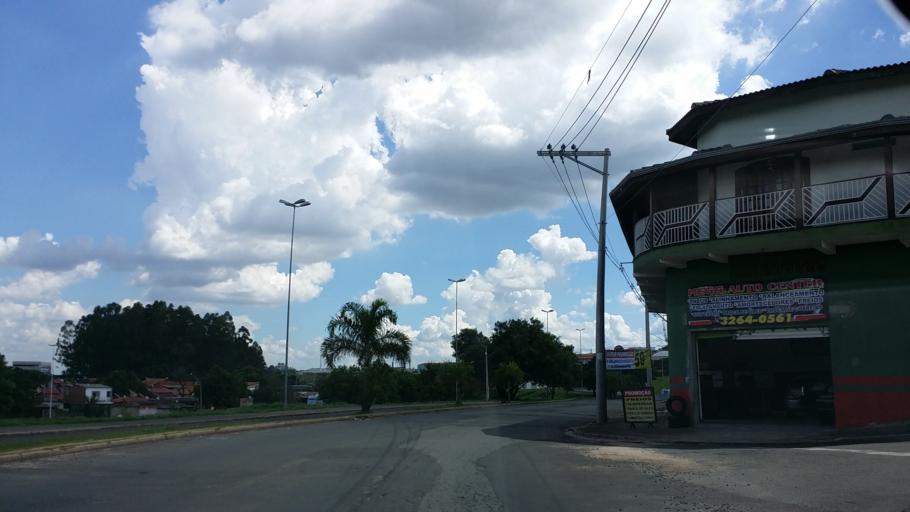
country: BR
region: Sao Paulo
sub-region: Indaiatuba
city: Indaiatuba
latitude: -23.1295
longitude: -47.2348
